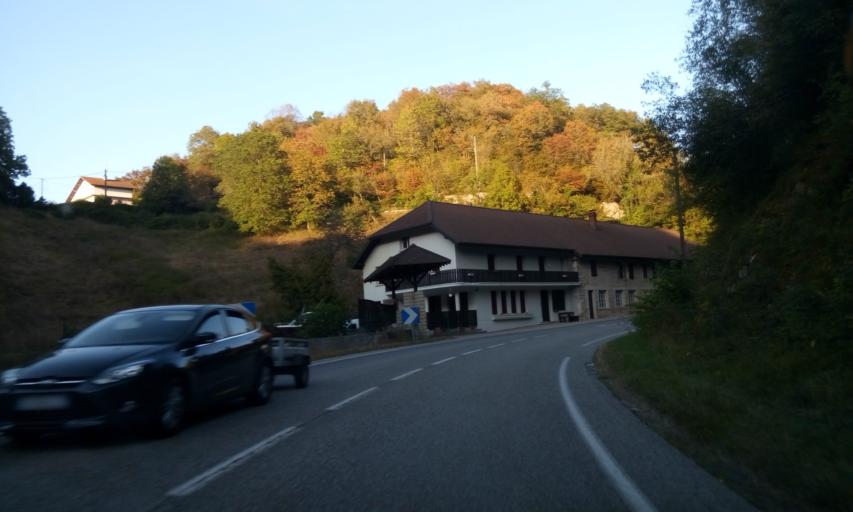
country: FR
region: Rhone-Alpes
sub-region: Departement de l'Ain
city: Saint-Martin-du-Frene
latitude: 46.1171
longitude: 5.4985
